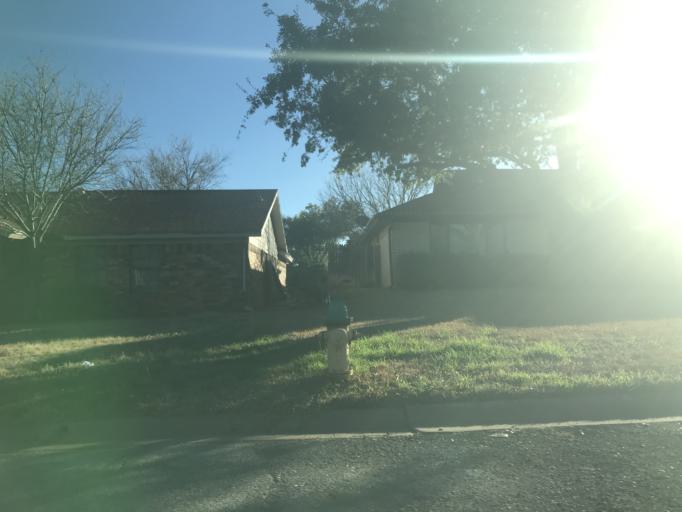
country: US
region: Texas
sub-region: Tom Green County
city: San Angelo
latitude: 31.4262
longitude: -100.4919
